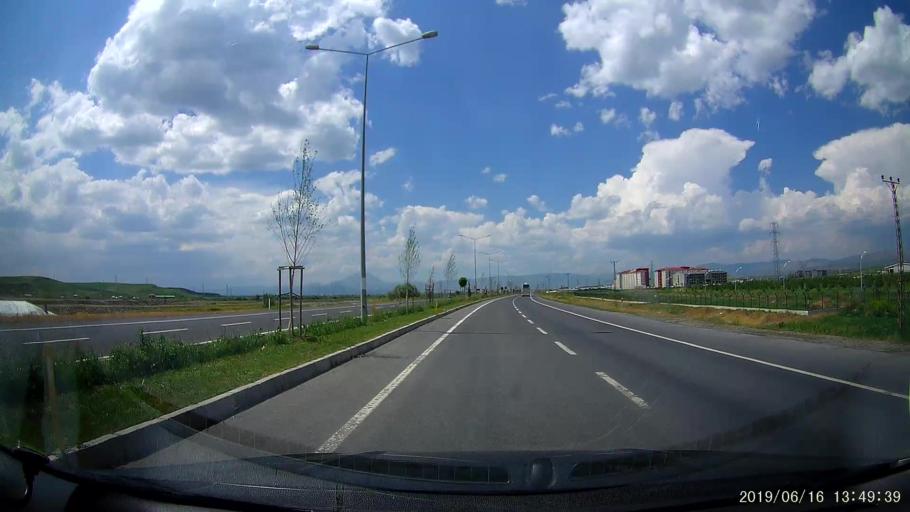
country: TR
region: Agri
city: Agri
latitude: 39.7189
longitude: 42.9880
